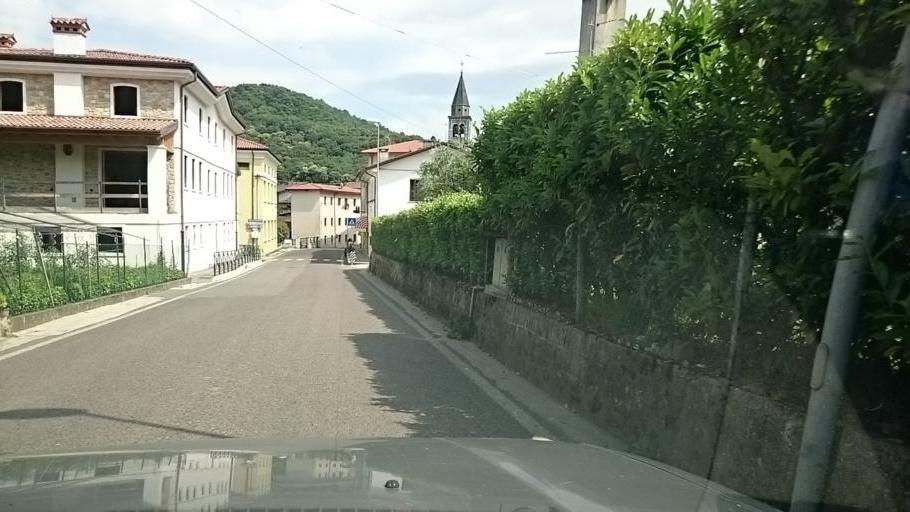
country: IT
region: Veneto
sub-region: Provincia di Vicenza
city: Marostica
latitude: 45.7626
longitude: 11.6442
